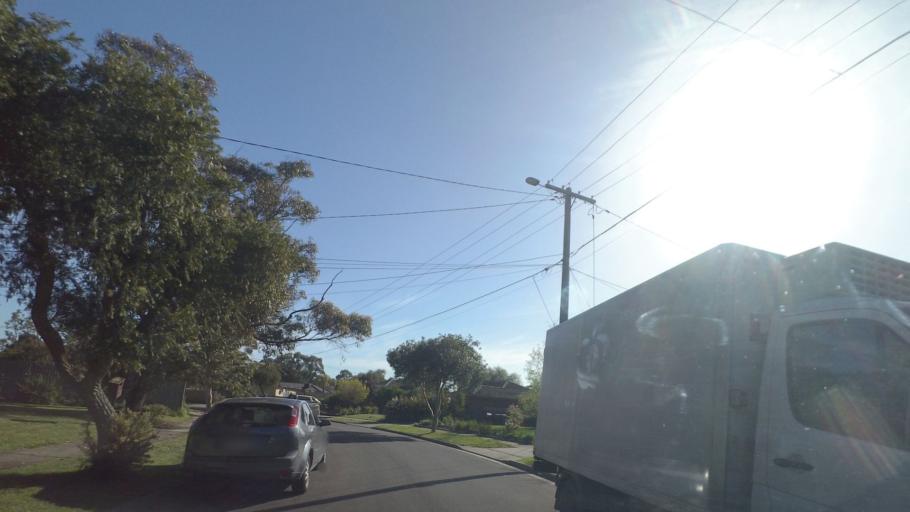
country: AU
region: Victoria
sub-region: Maroondah
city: Heathmont
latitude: -37.8384
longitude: 145.2539
